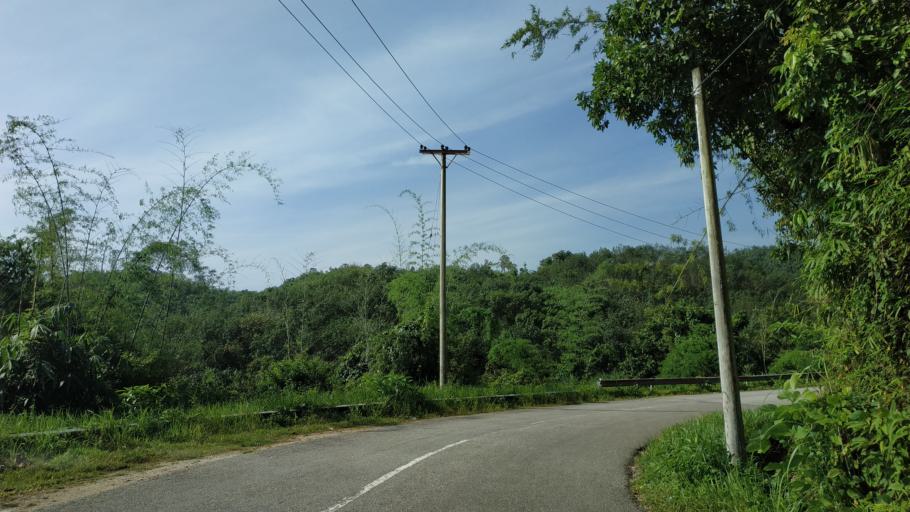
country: TH
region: Kanchanaburi
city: Thong Pha Phum
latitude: 14.6268
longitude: 98.1309
